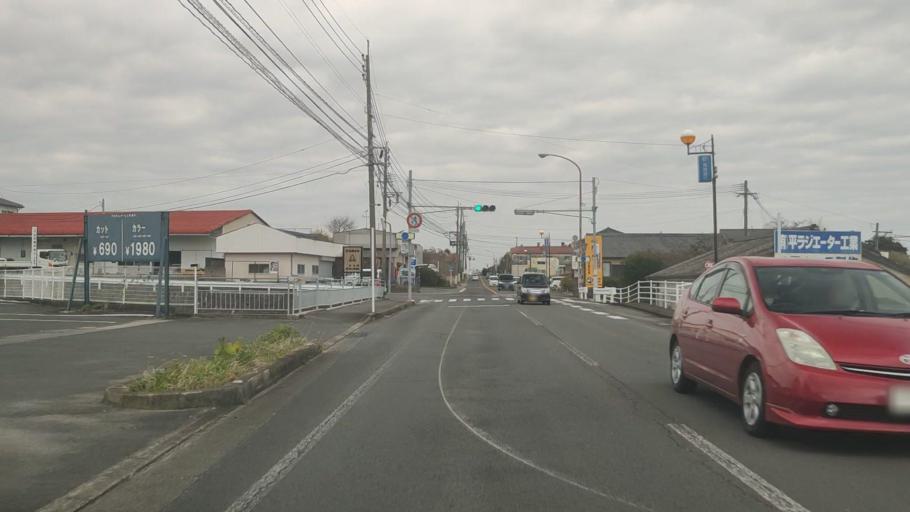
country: JP
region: Nagasaki
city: Shimabara
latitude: 32.8286
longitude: 130.3498
